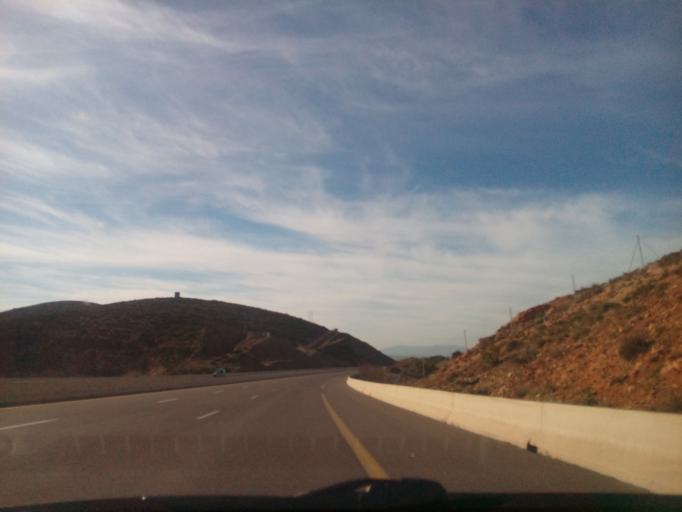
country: DZ
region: Tlemcen
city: Beni Mester
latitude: 34.9118
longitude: -1.3997
